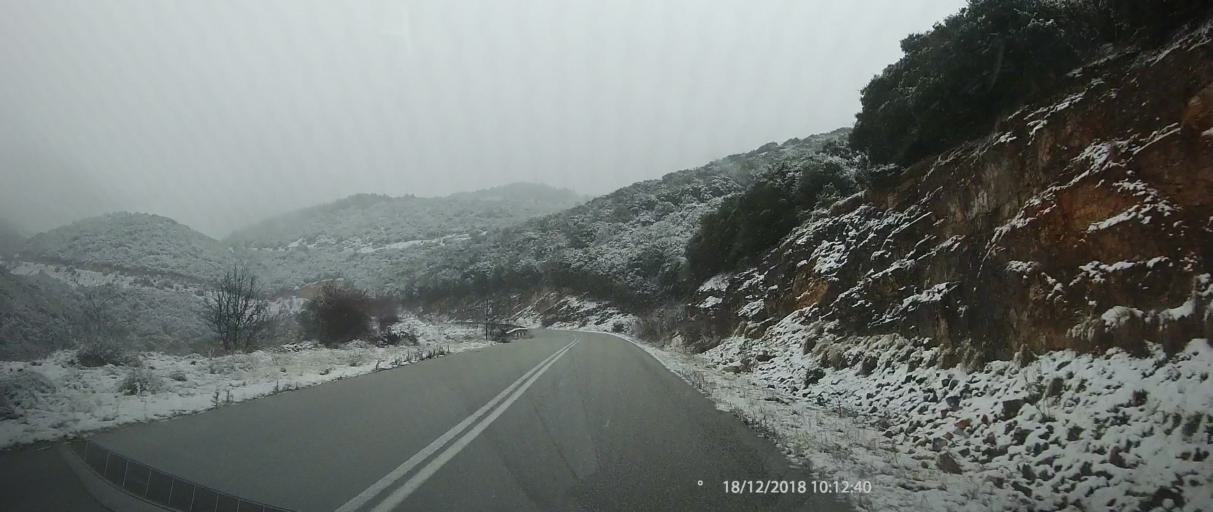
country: GR
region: Thessaly
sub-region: Nomos Larisis
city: Livadi
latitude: 40.1004
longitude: 22.2081
